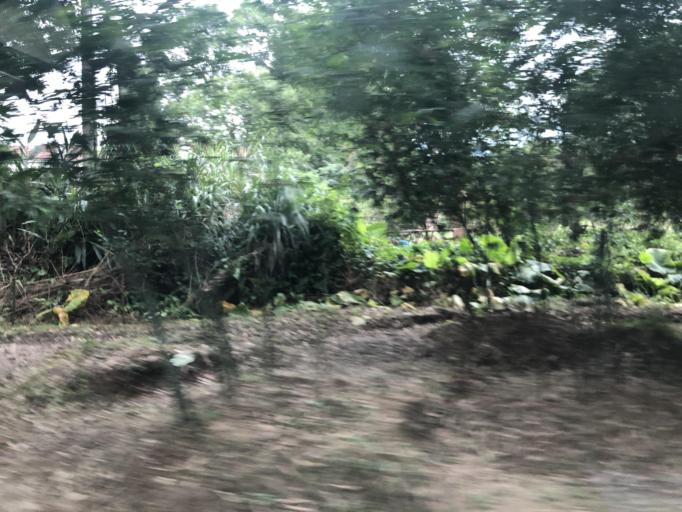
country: TW
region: Taiwan
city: Daxi
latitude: 24.9182
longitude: 121.3627
